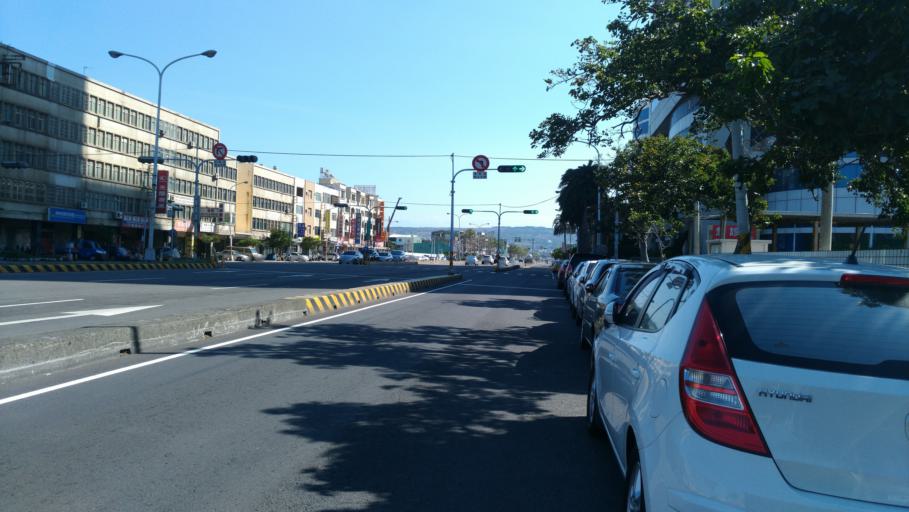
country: TW
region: Taiwan
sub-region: Taichung City
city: Taichung
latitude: 24.2478
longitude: 120.5418
